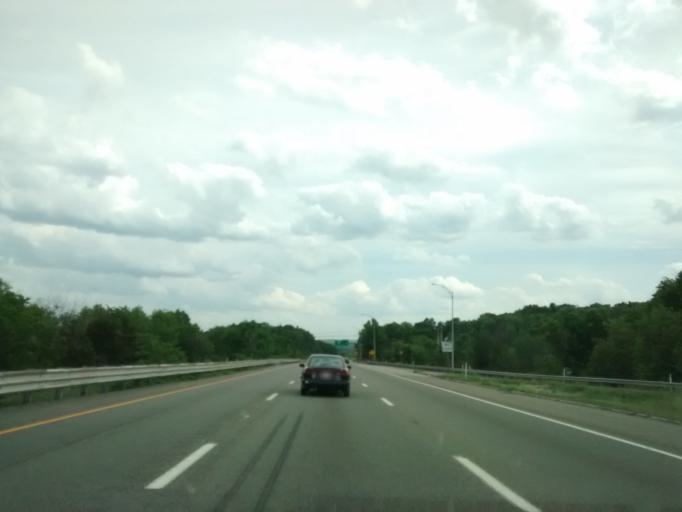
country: US
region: Massachusetts
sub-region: Worcester County
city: Southborough
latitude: 42.2906
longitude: -71.5678
